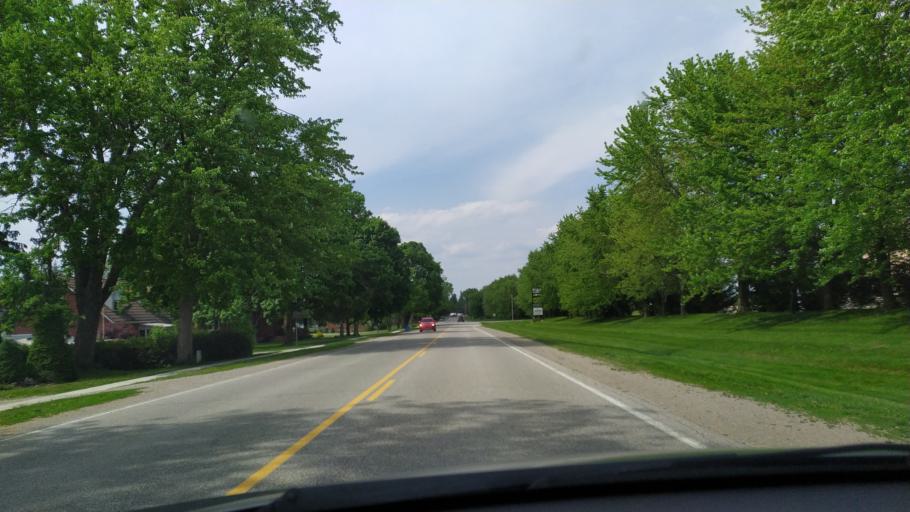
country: CA
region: Ontario
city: Ingersoll
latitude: 42.9851
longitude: -80.9525
